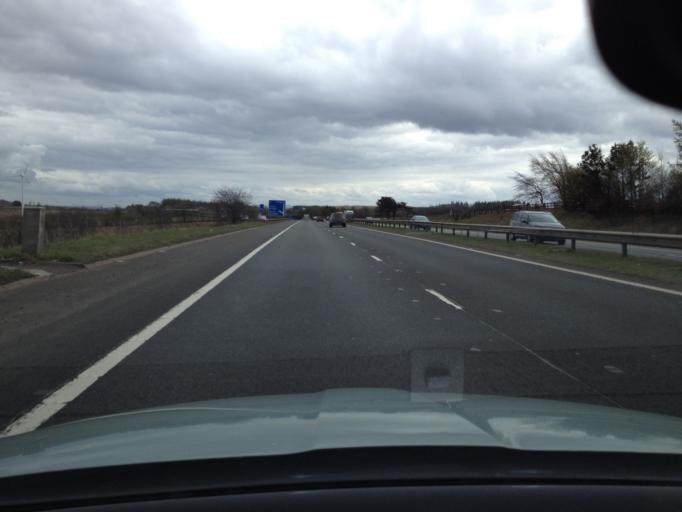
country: GB
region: Scotland
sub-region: North Lanarkshire
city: Shotts
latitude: 55.8553
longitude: -3.8182
